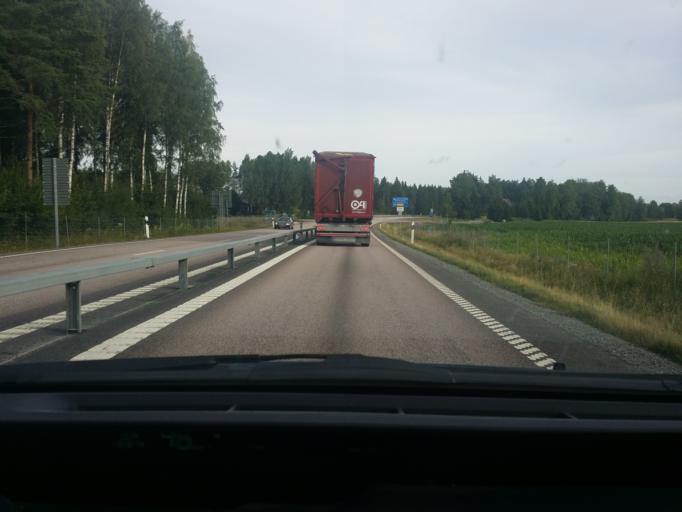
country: SE
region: Vaestmanland
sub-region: Sala Kommun
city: Sala
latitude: 59.8294
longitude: 16.5317
